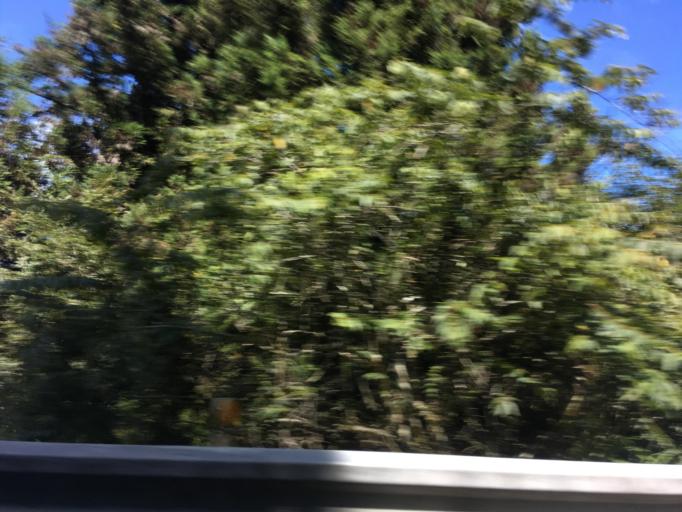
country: TW
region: Taiwan
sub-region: Yilan
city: Yilan
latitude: 24.5063
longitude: 121.5256
